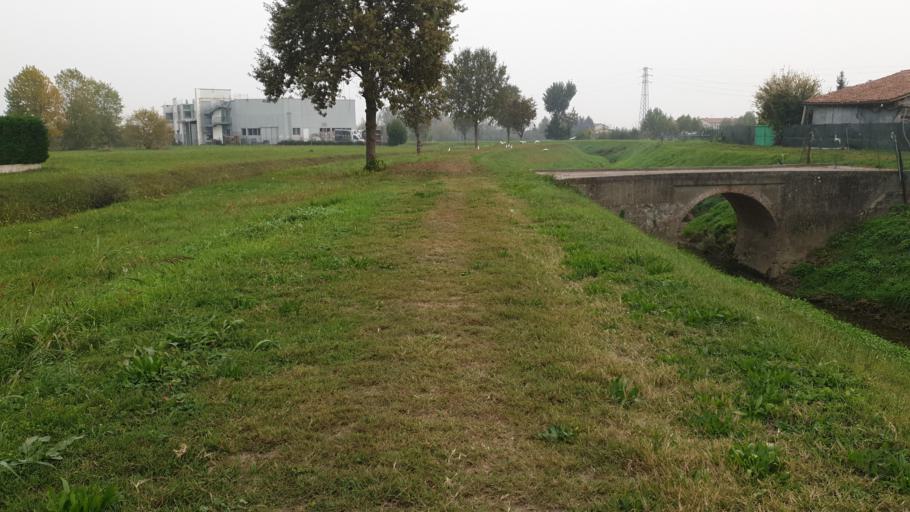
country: IT
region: Veneto
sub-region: Provincia di Padova
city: Casalserugo
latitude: 45.3063
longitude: 11.9117
